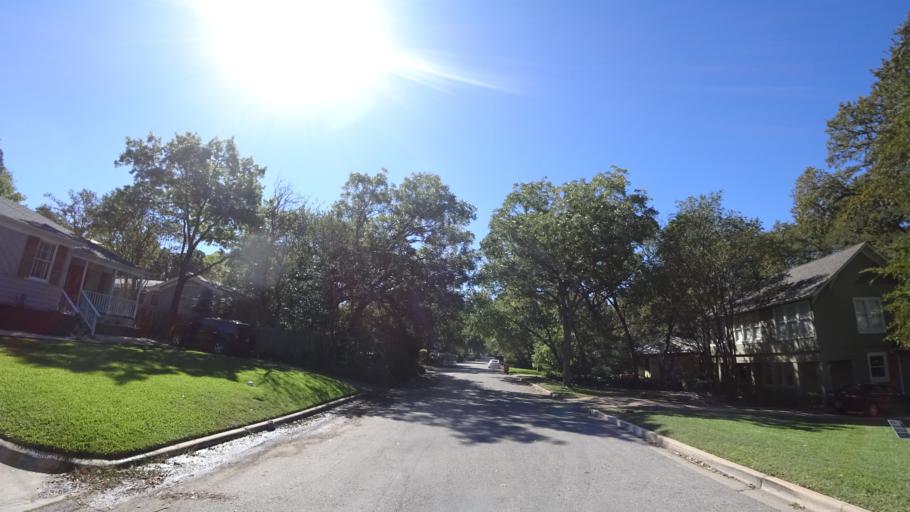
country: US
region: Texas
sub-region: Travis County
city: Rollingwood
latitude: 30.2943
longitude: -97.7672
